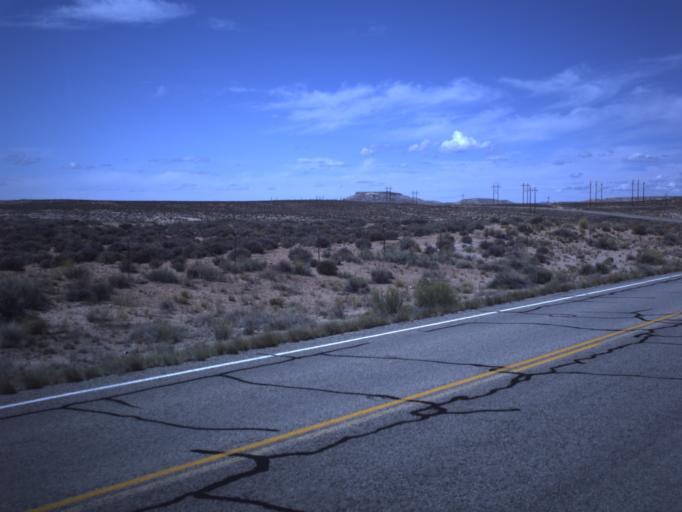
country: US
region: Utah
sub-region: San Juan County
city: Blanding
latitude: 37.2764
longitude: -109.3604
